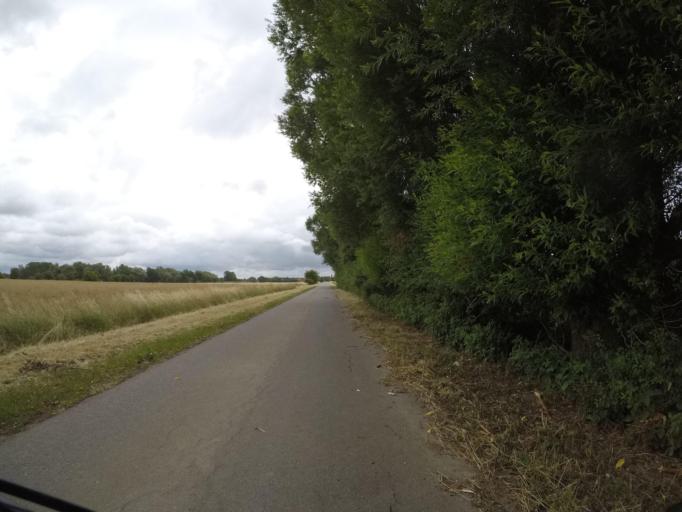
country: DE
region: Lower Saxony
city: Damnatz
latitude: 53.1728
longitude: 11.1210
